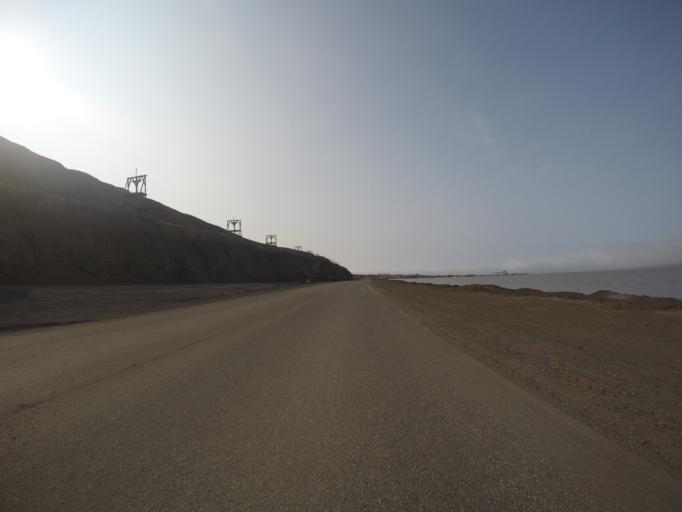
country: SJ
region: Svalbard
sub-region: Spitsbergen
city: Longyearbyen
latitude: 78.2318
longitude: 15.5721
